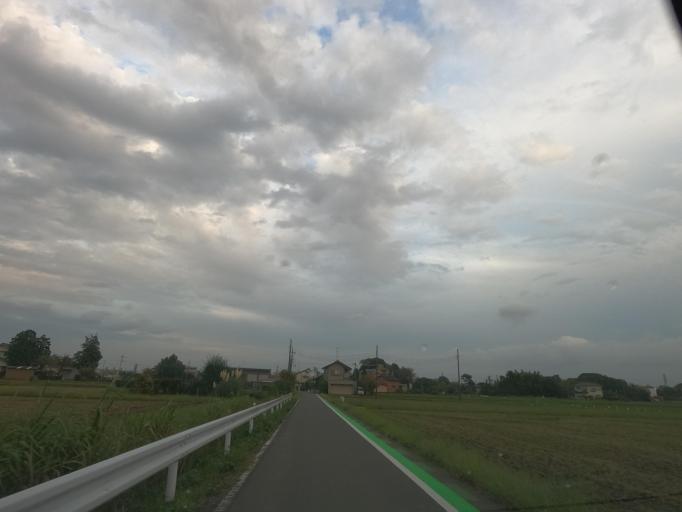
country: JP
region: Saitama
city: Shiki
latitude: 35.8512
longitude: 139.5750
